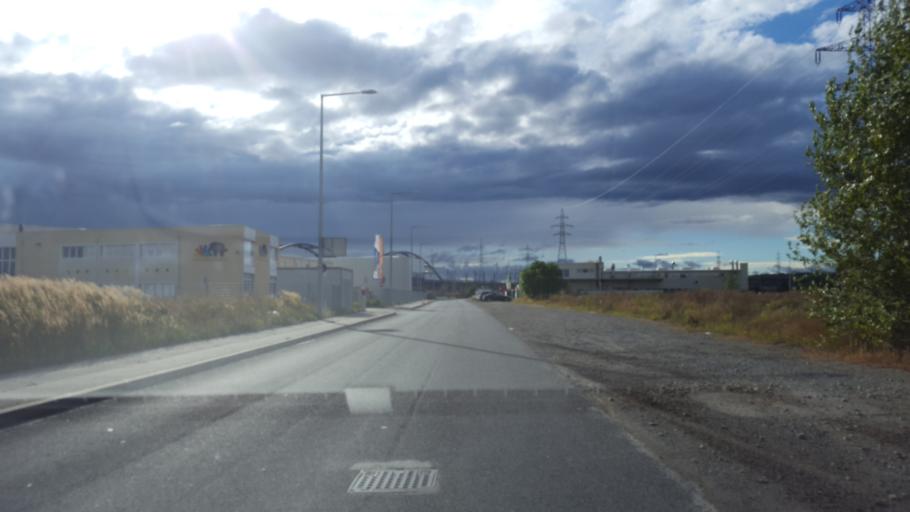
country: AT
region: Lower Austria
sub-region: Politischer Bezirk Wien-Umgebung
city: Schwechat
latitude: 48.1403
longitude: 16.4405
